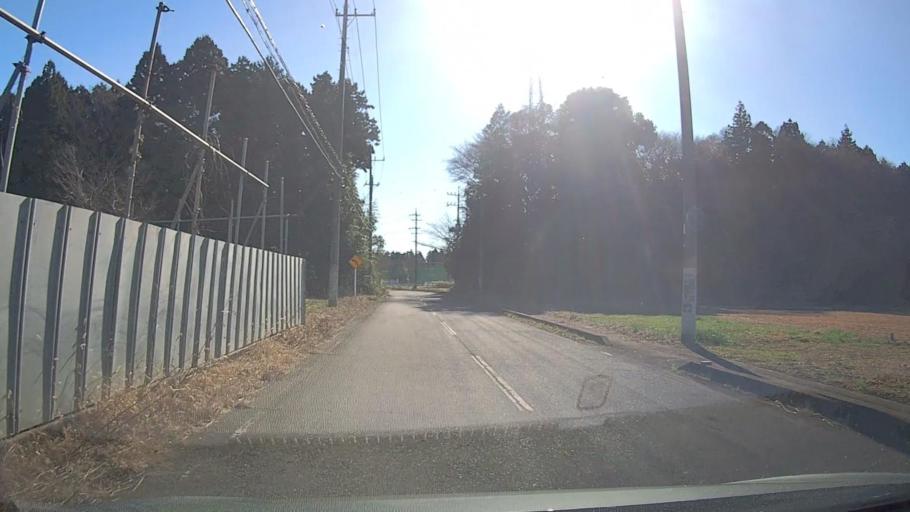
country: JP
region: Ibaraki
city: Mito-shi
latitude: 36.4412
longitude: 140.4412
